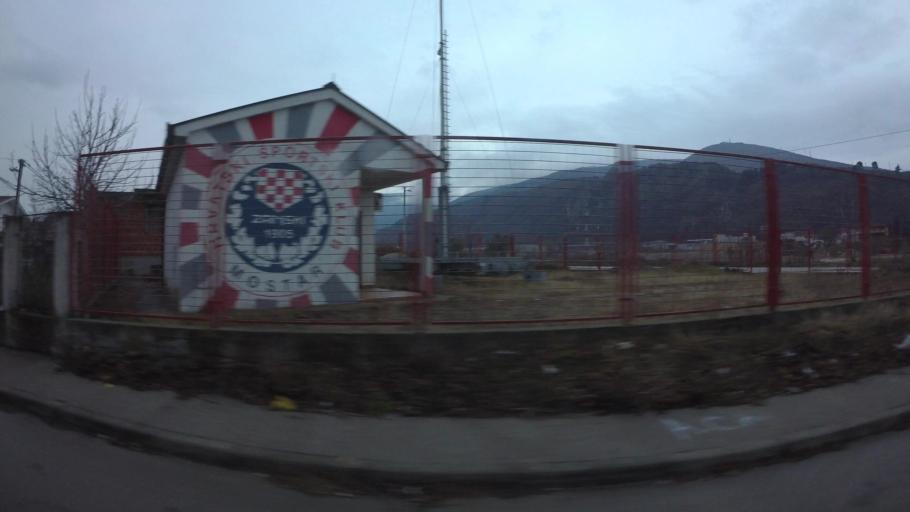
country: BA
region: Federation of Bosnia and Herzegovina
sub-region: Hercegovacko-Bosanski Kanton
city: Mostar
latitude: 43.3666
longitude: 17.8177
